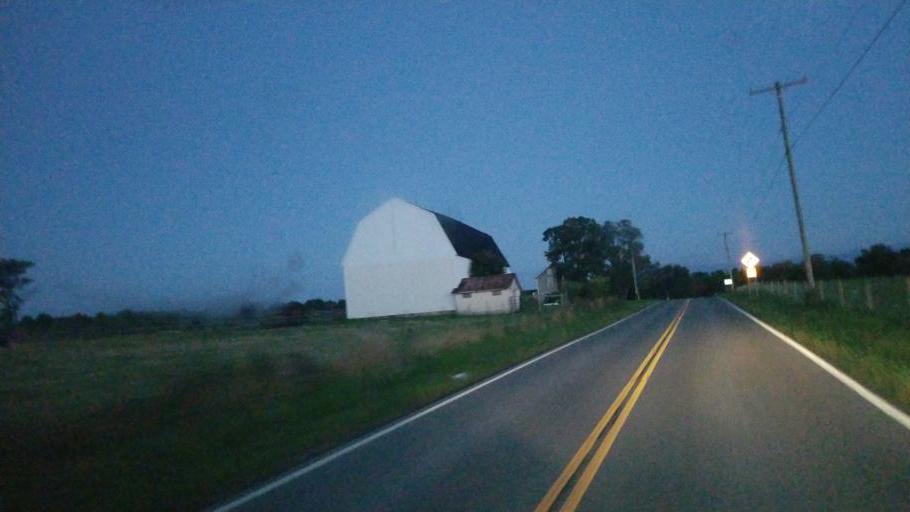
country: US
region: Ohio
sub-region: Ashland County
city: Ashland
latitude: 40.8688
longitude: -82.4053
